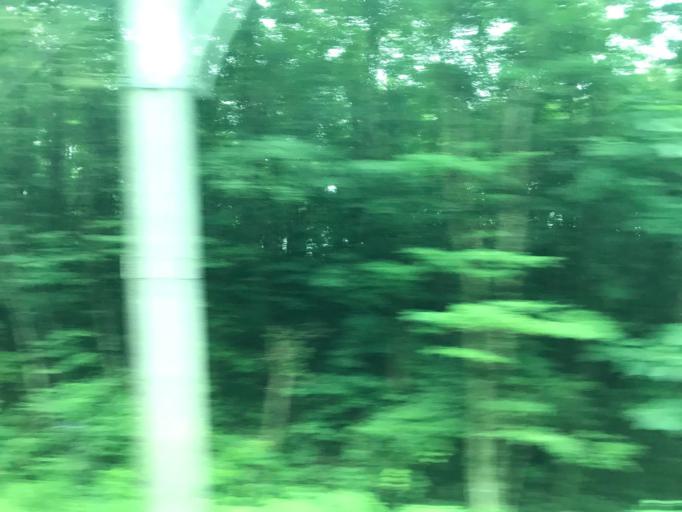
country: JP
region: Tochigi
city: Kuroiso
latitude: 37.0417
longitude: 140.1507
